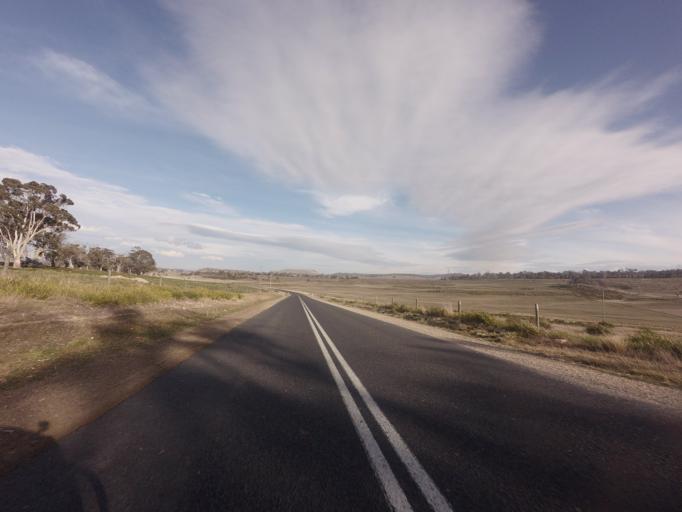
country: AU
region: Tasmania
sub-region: Derwent Valley
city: New Norfolk
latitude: -42.2461
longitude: 146.9257
